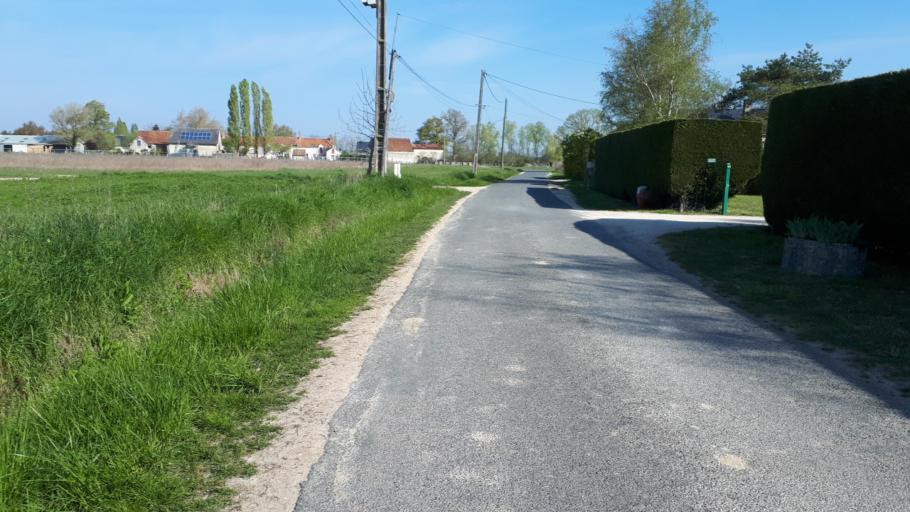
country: FR
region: Centre
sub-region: Departement du Loir-et-Cher
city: Contres
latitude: 47.3788
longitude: 1.3937
